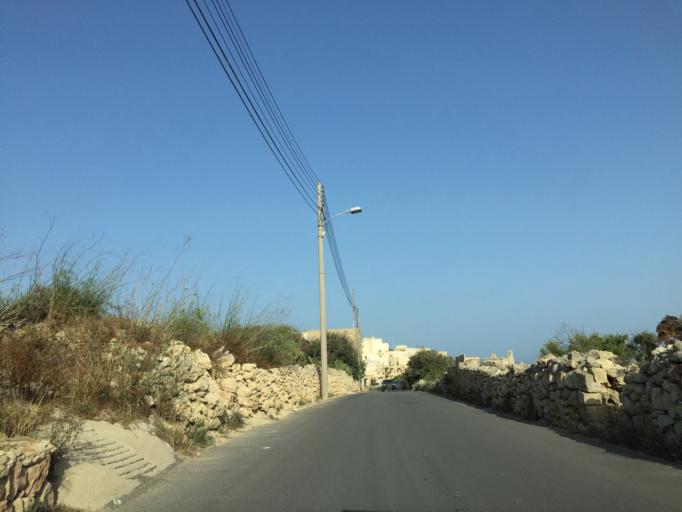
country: MT
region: Il-Qala
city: Qala
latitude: 36.0359
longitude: 14.3174
